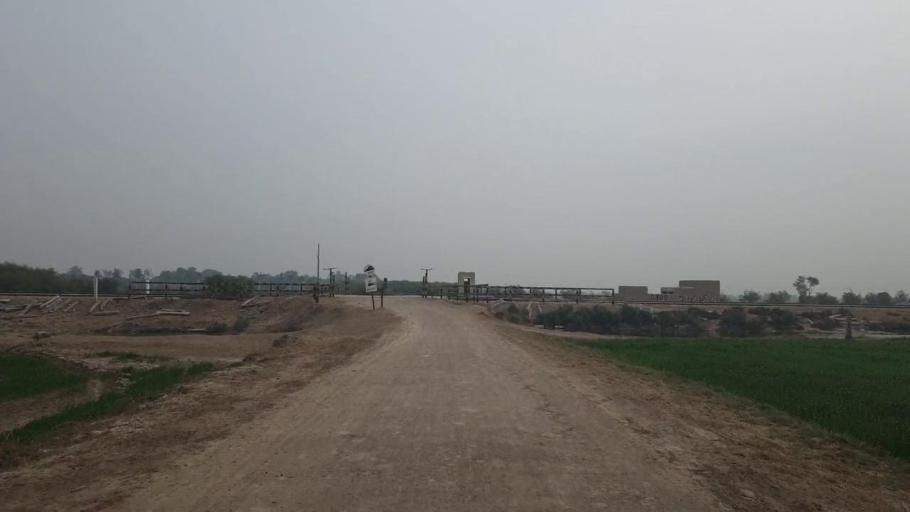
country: PK
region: Sindh
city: Tando Adam
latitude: 25.8127
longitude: 68.6628
